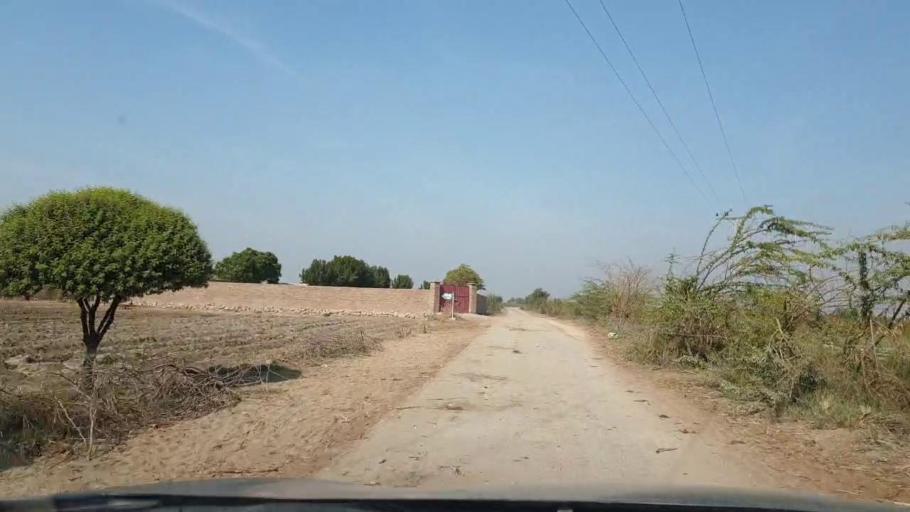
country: PK
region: Sindh
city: Berani
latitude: 25.6941
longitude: 68.7535
